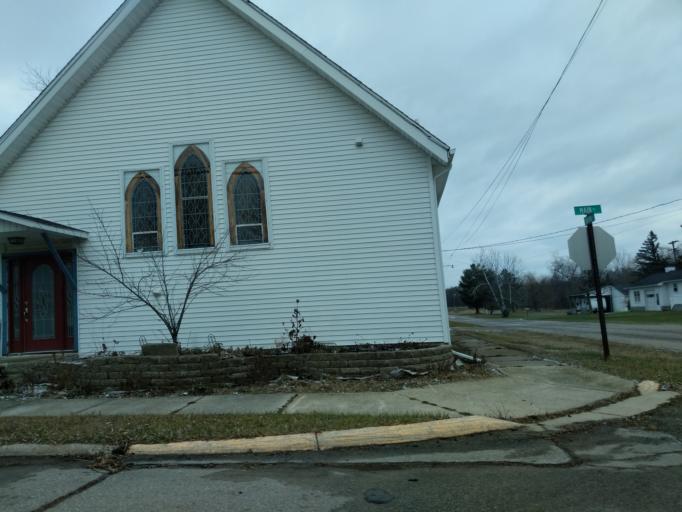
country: US
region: Michigan
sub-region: Lapeer County
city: North Branch
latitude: 43.3125
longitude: -83.1791
